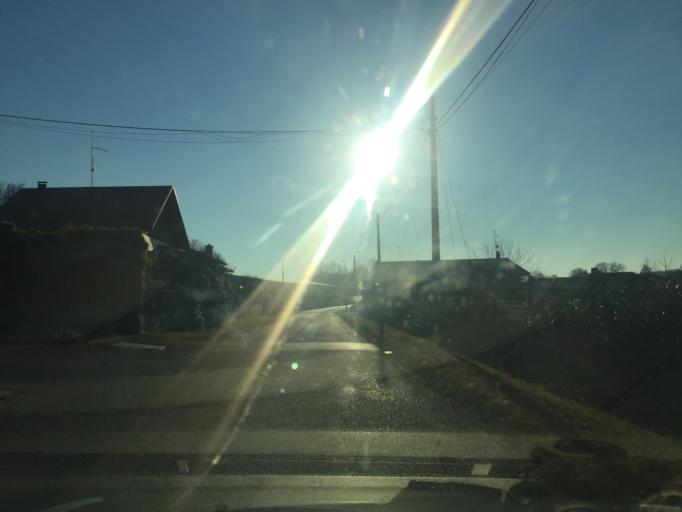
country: IT
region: Friuli Venezia Giulia
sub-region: Provincia di Udine
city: Buia
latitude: 46.2175
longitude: 13.1045
